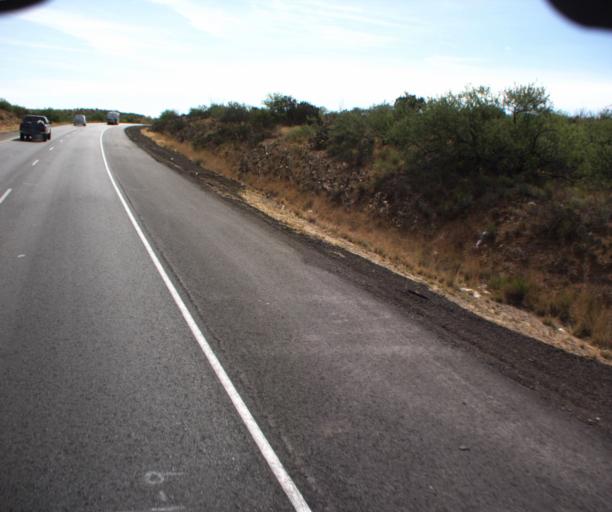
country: US
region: Arizona
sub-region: Pima County
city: Vail
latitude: 31.9983
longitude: -110.6286
